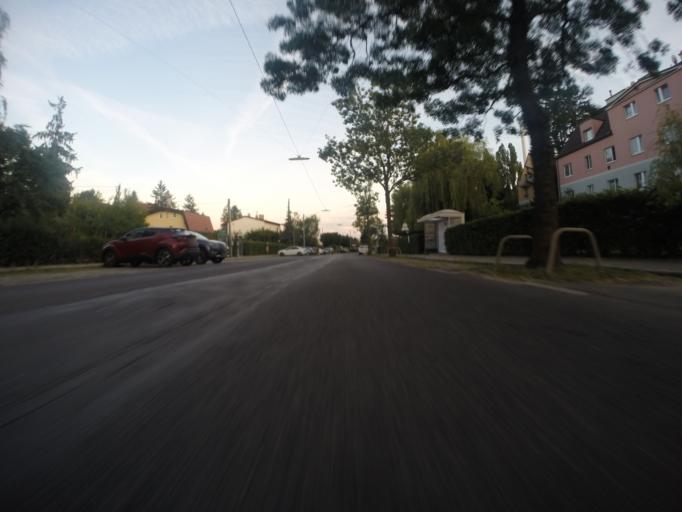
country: AT
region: Vienna
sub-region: Wien Stadt
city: Vienna
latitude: 48.2095
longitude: 16.2904
